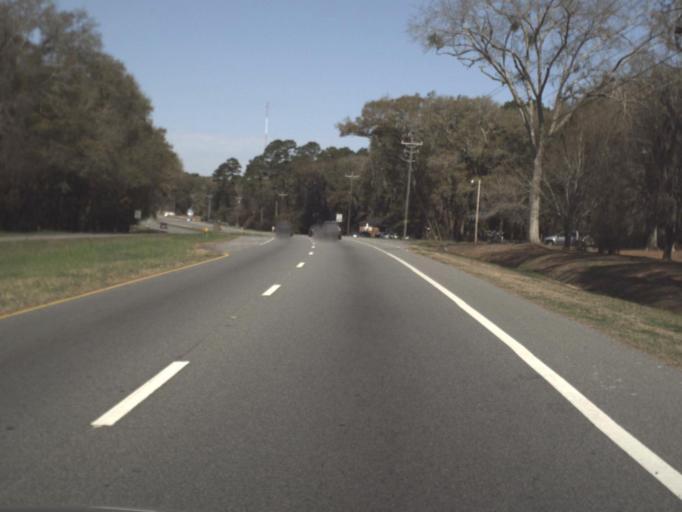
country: US
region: Florida
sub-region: Leon County
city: Tallahassee
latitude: 30.5047
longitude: -84.3307
